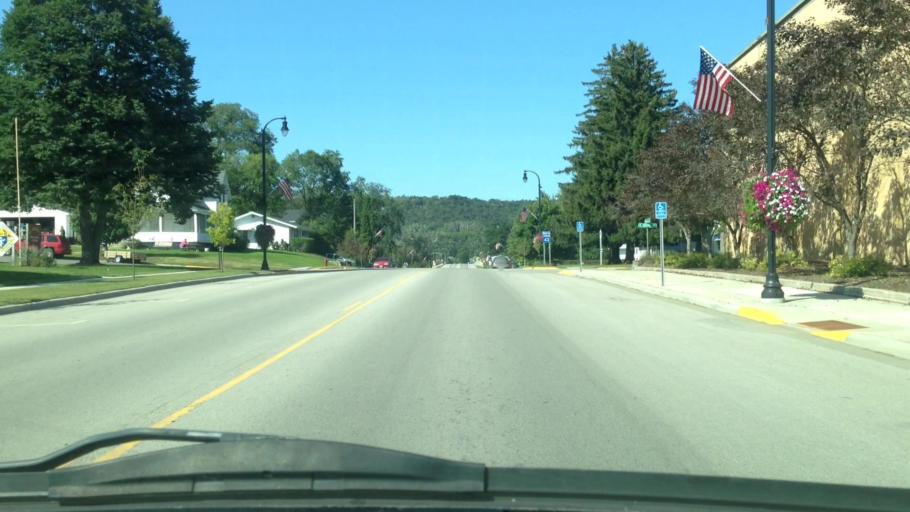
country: US
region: Minnesota
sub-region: Fillmore County
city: Rushford
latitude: 43.8111
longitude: -91.7532
